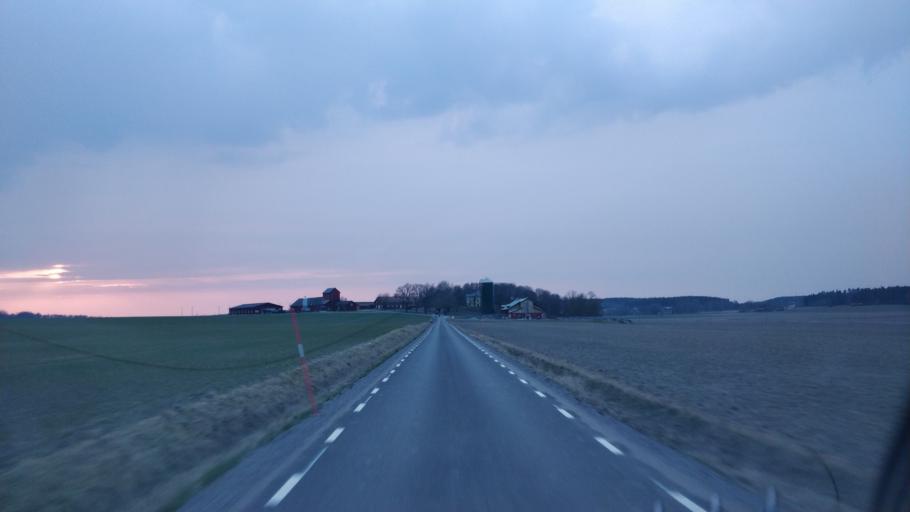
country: SE
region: Uppsala
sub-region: Enkopings Kommun
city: Orsundsbro
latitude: 59.7371
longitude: 17.1886
